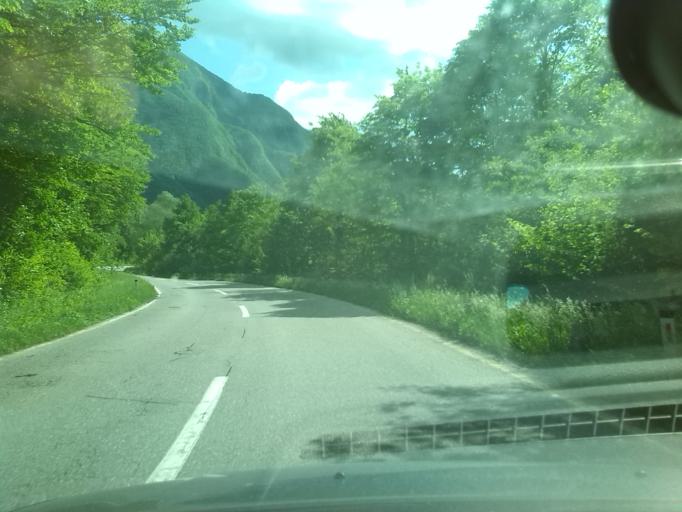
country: IT
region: Friuli Venezia Giulia
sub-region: Provincia di Udine
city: Pulfero
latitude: 46.2305
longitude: 13.5010
